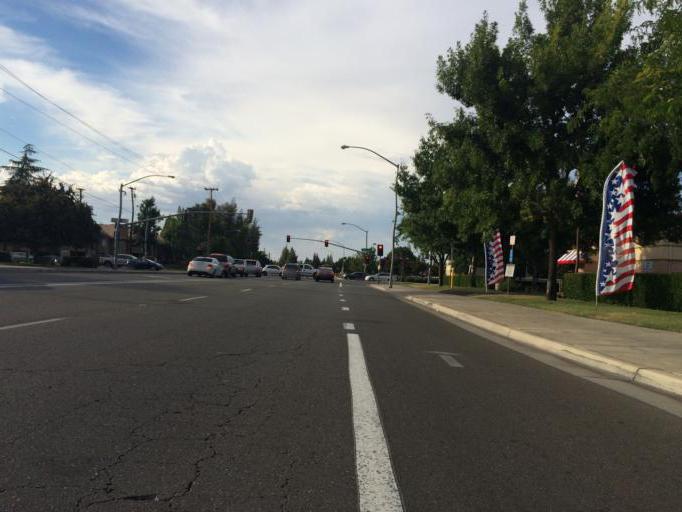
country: US
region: California
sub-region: Fresno County
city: Clovis
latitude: 36.8511
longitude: -119.7745
